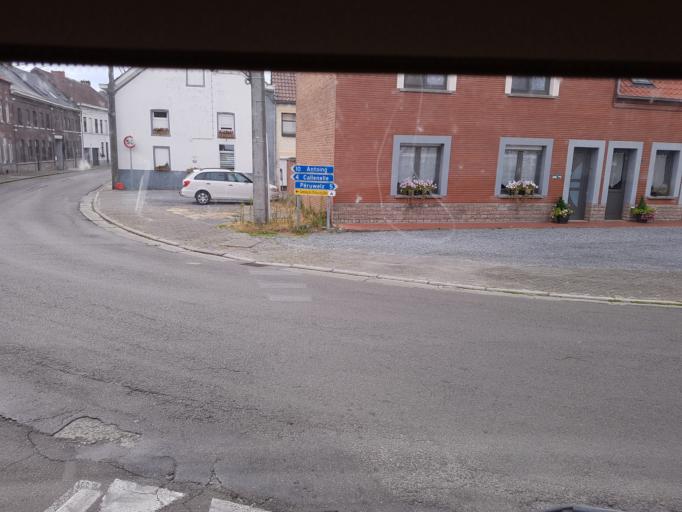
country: FR
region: Nord-Pas-de-Calais
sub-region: Departement du Nord
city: Hergnies
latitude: 50.5057
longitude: 3.5353
